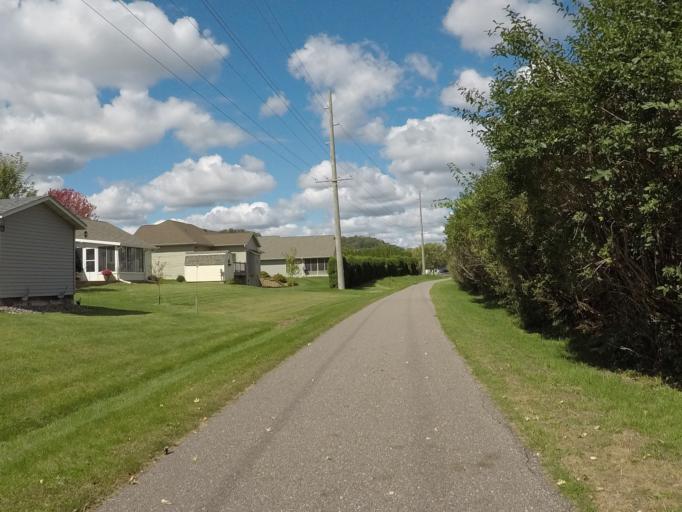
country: US
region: Wisconsin
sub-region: Richland County
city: Richland Center
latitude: 43.3215
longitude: -90.3803
